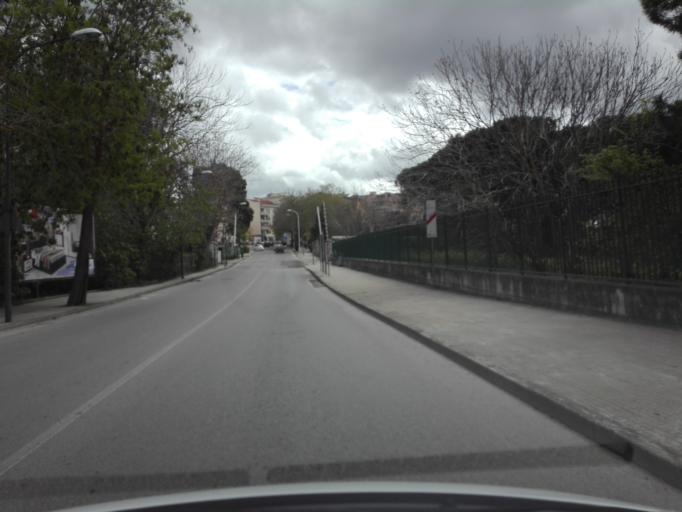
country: IT
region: Sardinia
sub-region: Provincia di Sassari
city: Sassari
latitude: 40.7385
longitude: 8.5590
